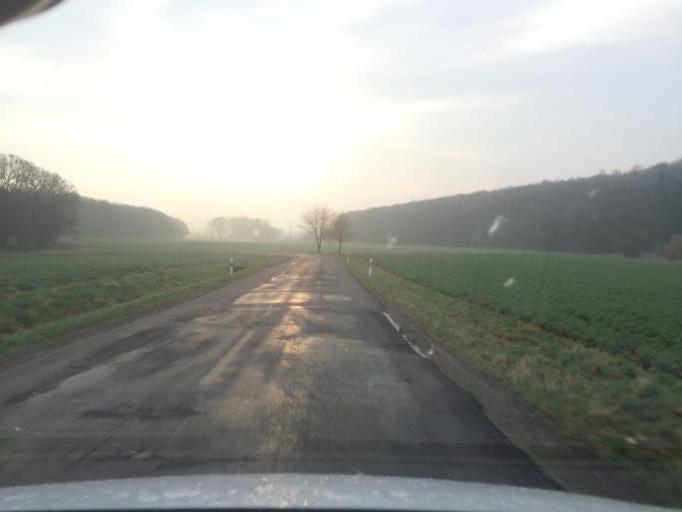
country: DE
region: Thuringia
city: Bischofferode
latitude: 51.5278
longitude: 10.4662
